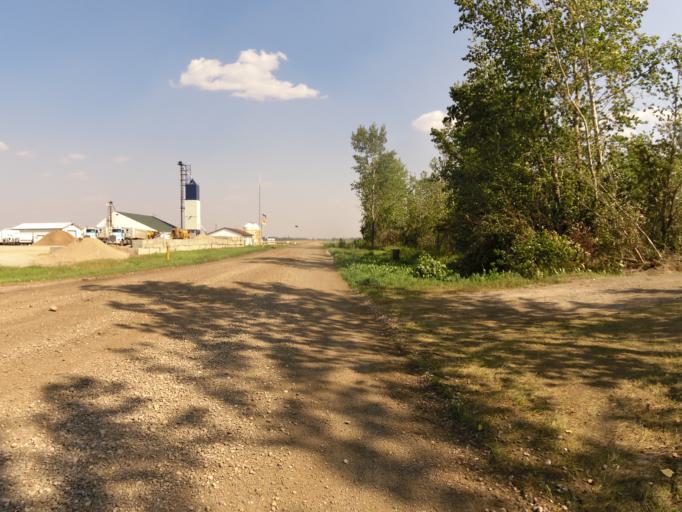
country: US
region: North Dakota
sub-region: Walsh County
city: Grafton
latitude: 48.4307
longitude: -97.4015
